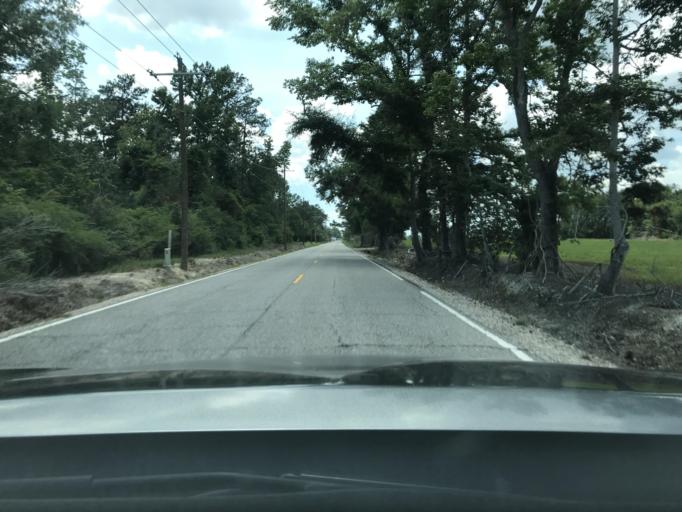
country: US
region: Louisiana
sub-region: Calcasieu Parish
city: Moss Bluff
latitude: 30.3300
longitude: -93.1618
